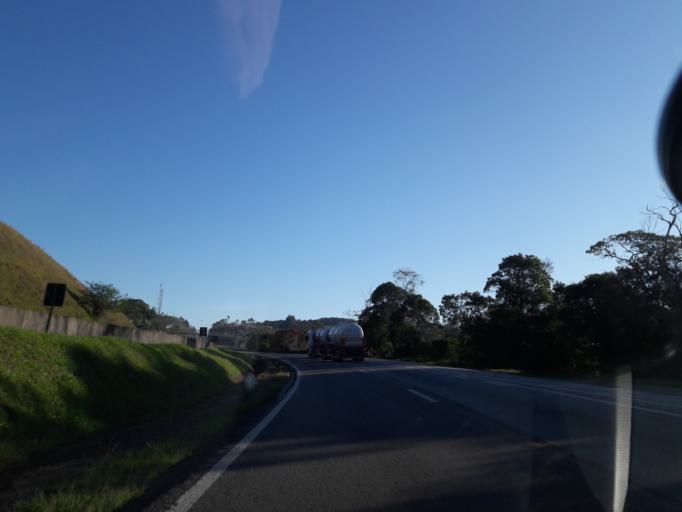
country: BR
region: Sao Paulo
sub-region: Juquitiba
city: Juquitiba
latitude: -23.9768
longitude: -47.1439
